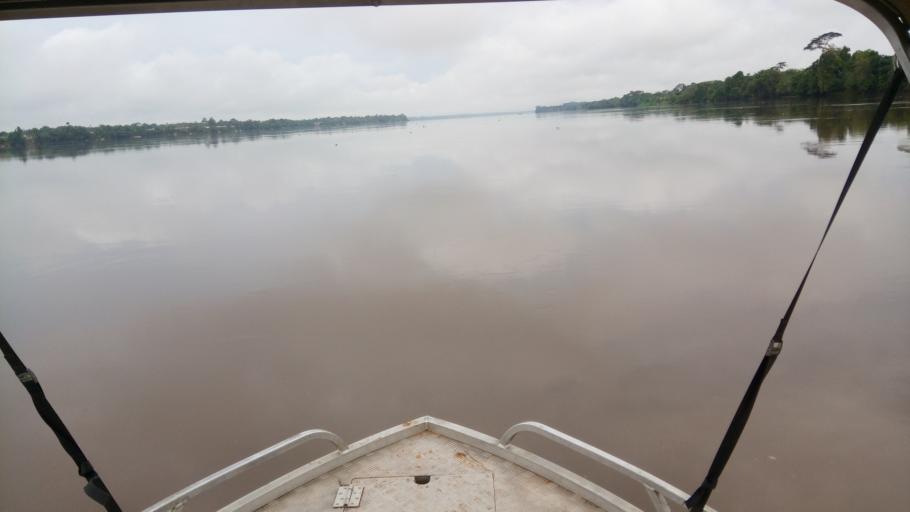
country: CD
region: Eastern Province
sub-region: Sous-Region de la Tshopo
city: Yangambi
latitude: 0.6601
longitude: 24.6302
